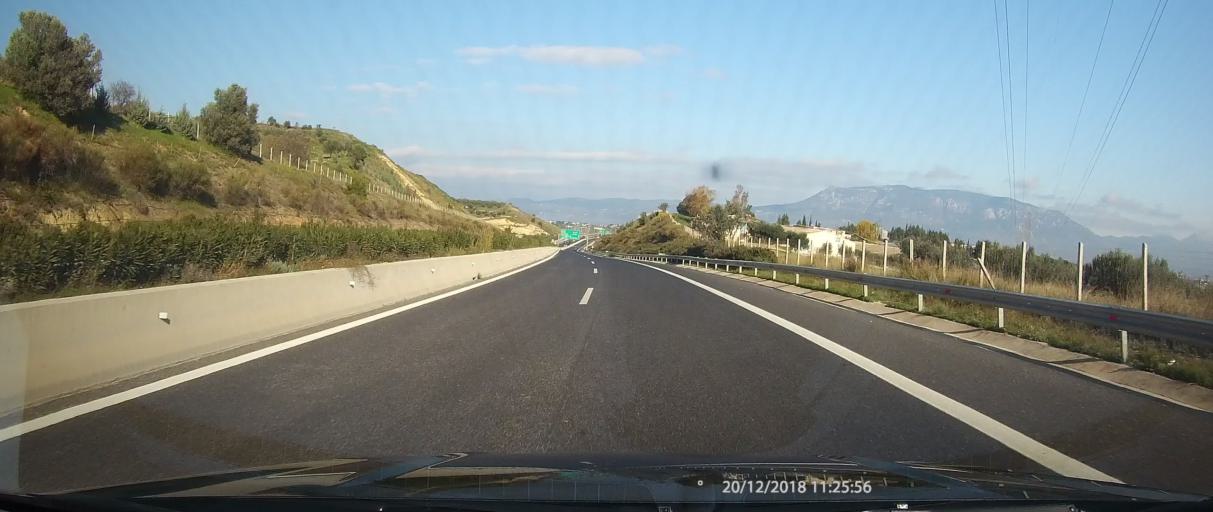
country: GR
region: Peloponnese
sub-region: Nomos Korinthias
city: Arkhaia Korinthos
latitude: 37.9073
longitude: 22.9061
